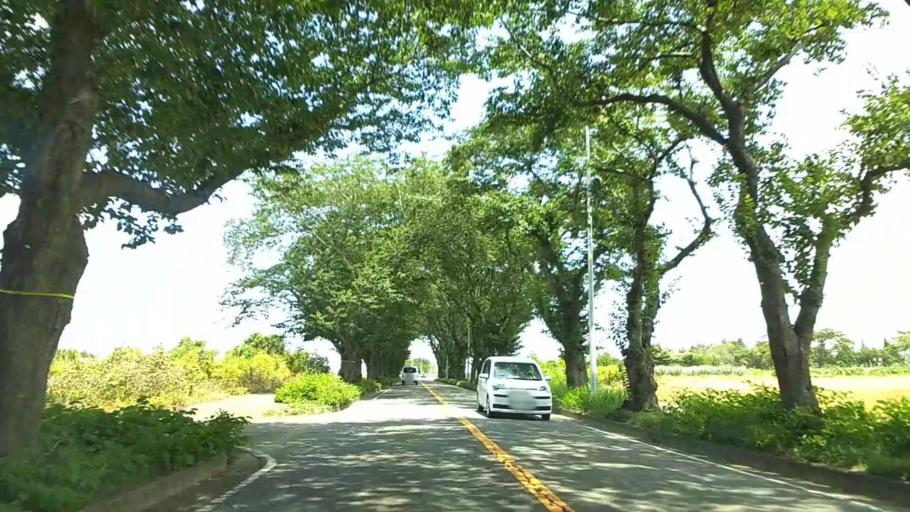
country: JP
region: Kanagawa
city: Minami-rinkan
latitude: 35.4929
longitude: 139.4801
